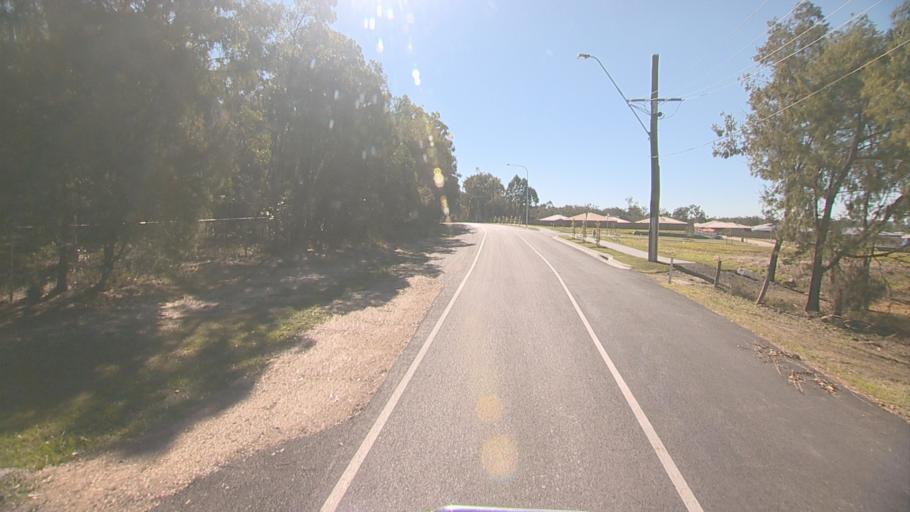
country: AU
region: Queensland
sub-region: Logan
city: Logan Reserve
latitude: -27.7145
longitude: 153.0766
